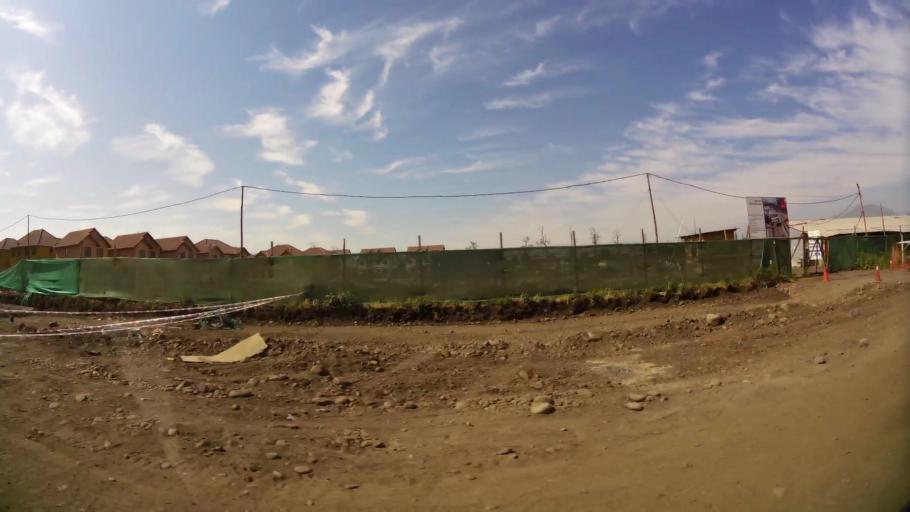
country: CL
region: Santiago Metropolitan
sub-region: Provincia de Talagante
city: Talagante
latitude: -33.6709
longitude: -70.9466
